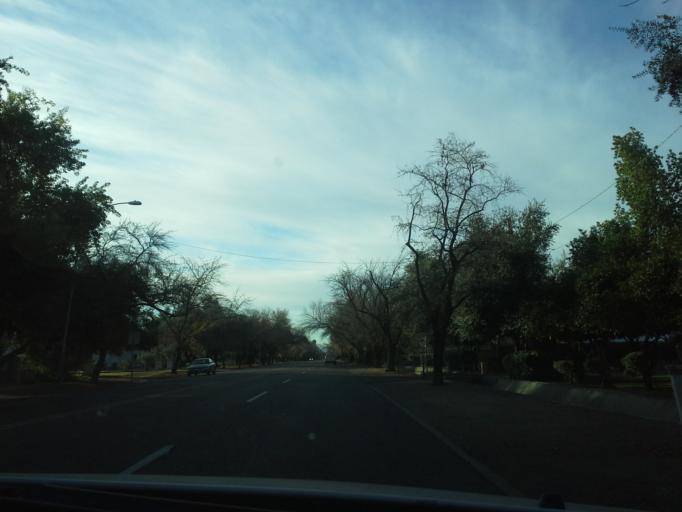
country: US
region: Arizona
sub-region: Maricopa County
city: Phoenix
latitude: 33.5509
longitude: -112.0740
